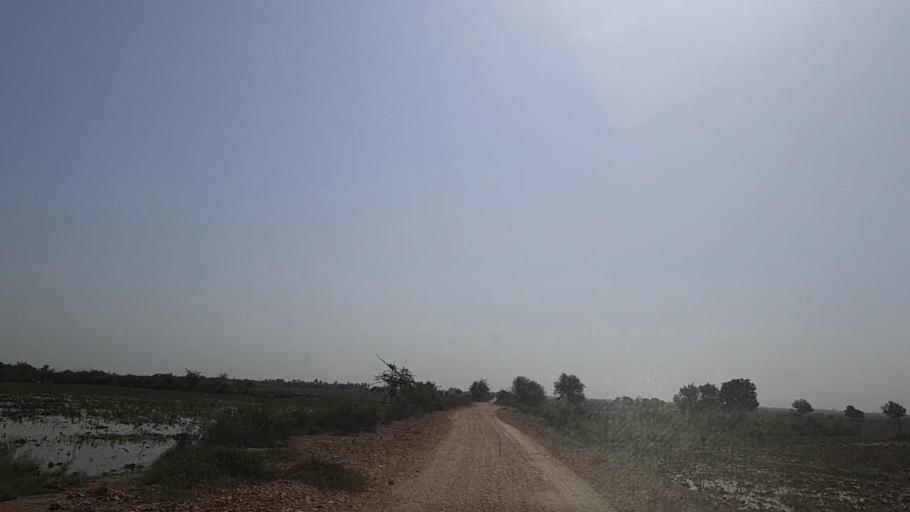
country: PK
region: Sindh
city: Daro Mehar
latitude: 24.7167
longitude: 68.1178
